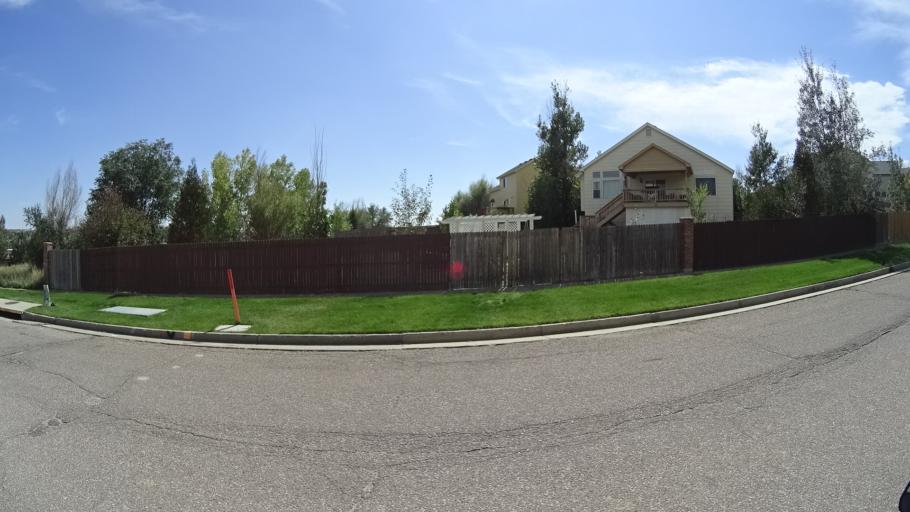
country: US
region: Colorado
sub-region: El Paso County
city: Cimarron Hills
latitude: 38.8994
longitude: -104.7116
